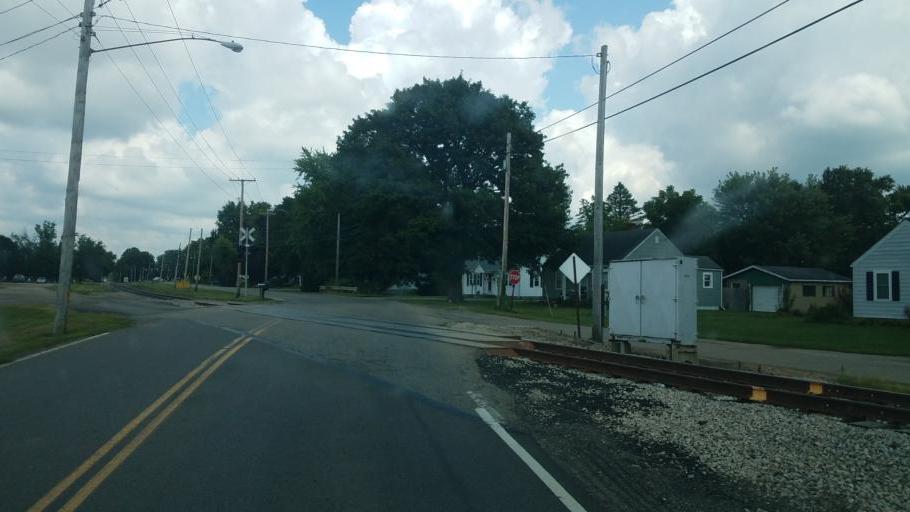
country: US
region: Ohio
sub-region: Knox County
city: Mount Vernon
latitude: 40.3719
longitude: -82.4880
